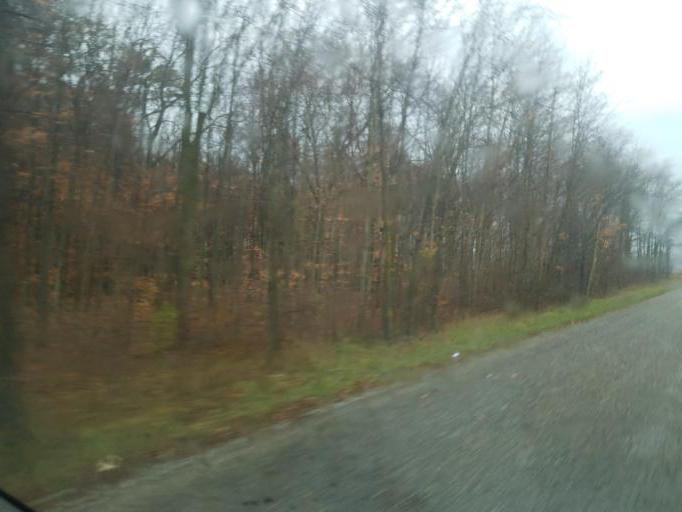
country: US
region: Ohio
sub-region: Morrow County
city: Cardington
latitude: 40.4697
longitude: -82.8800
